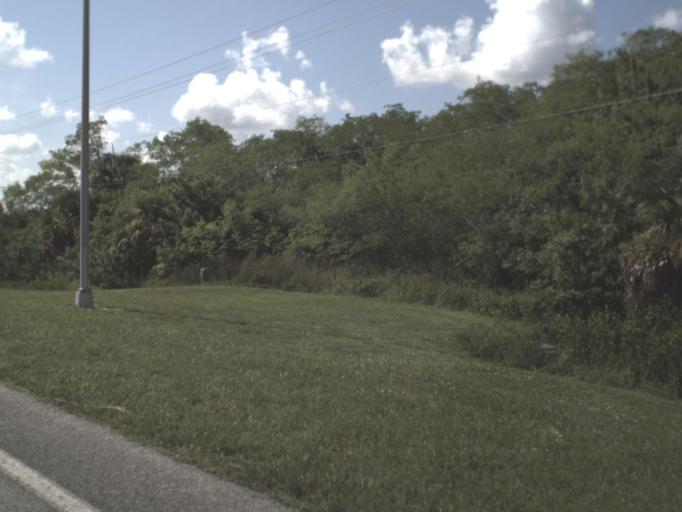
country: US
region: Florida
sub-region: Charlotte County
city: Charlotte Park
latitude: 26.9013
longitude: -82.0334
